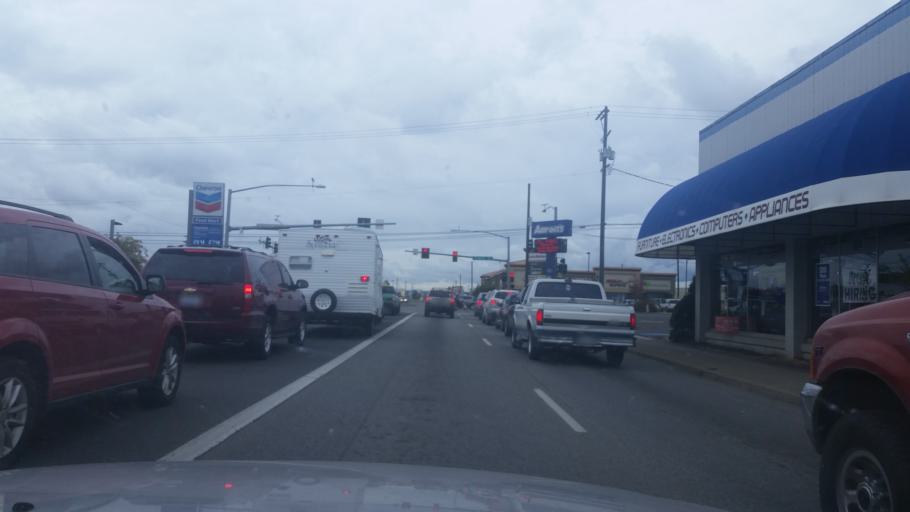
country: US
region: Washington
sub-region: Spokane County
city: Spokane
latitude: 47.6574
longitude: -117.3567
